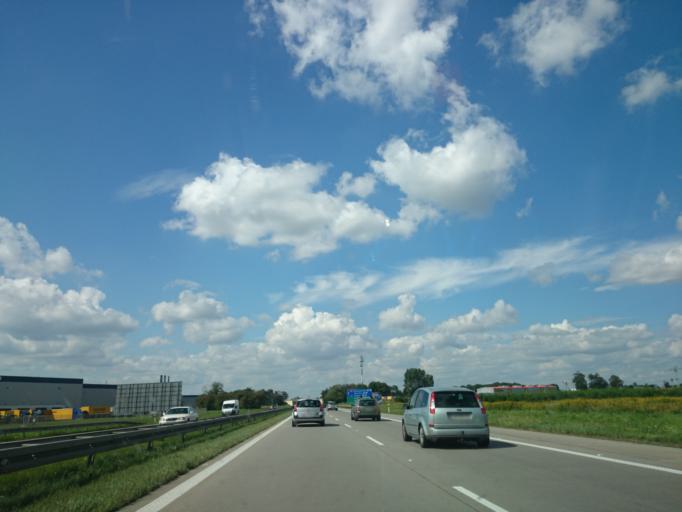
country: PL
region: Lower Silesian Voivodeship
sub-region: Powiat wroclawski
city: Tyniec Maly
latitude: 51.0388
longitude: 16.9021
